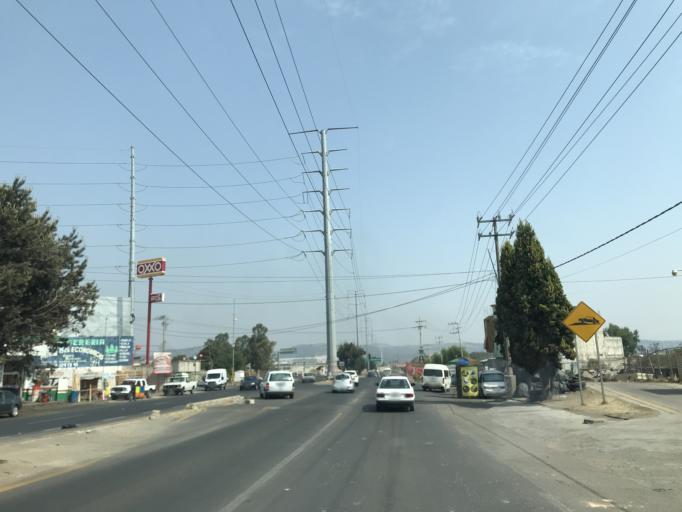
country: MX
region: Tlaxcala
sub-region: Chiautempan
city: Santa Cruz Tetela
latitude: 19.2994
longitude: -98.1960
